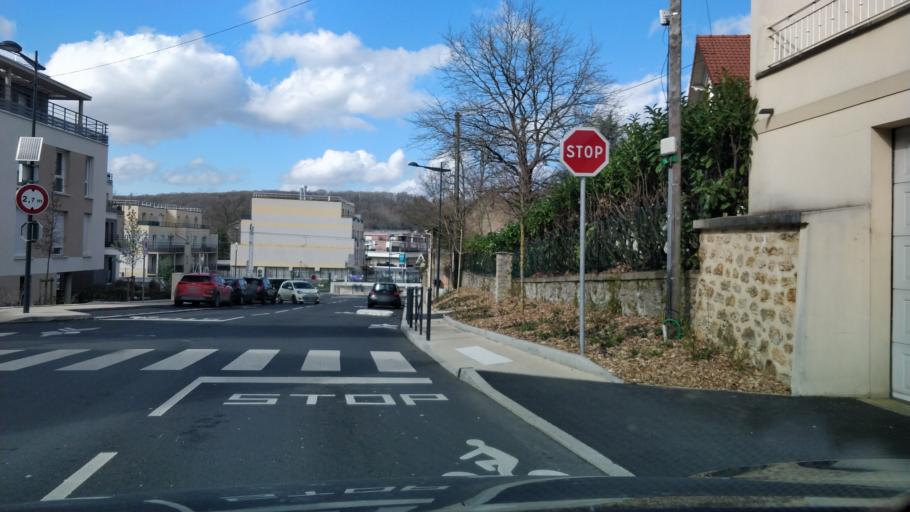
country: FR
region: Ile-de-France
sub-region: Departement de l'Essonne
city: Bures-sur-Yvette
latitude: 48.6949
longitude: 2.1637
